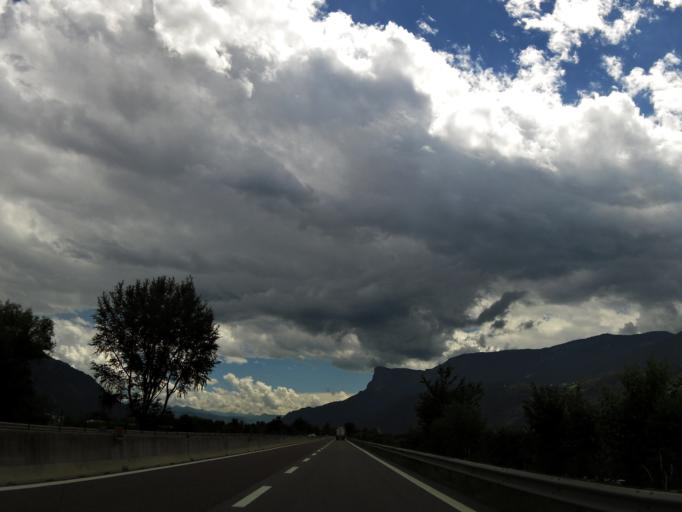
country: IT
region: Trentino-Alto Adige
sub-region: Bolzano
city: Postal
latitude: 46.6002
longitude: 11.1845
